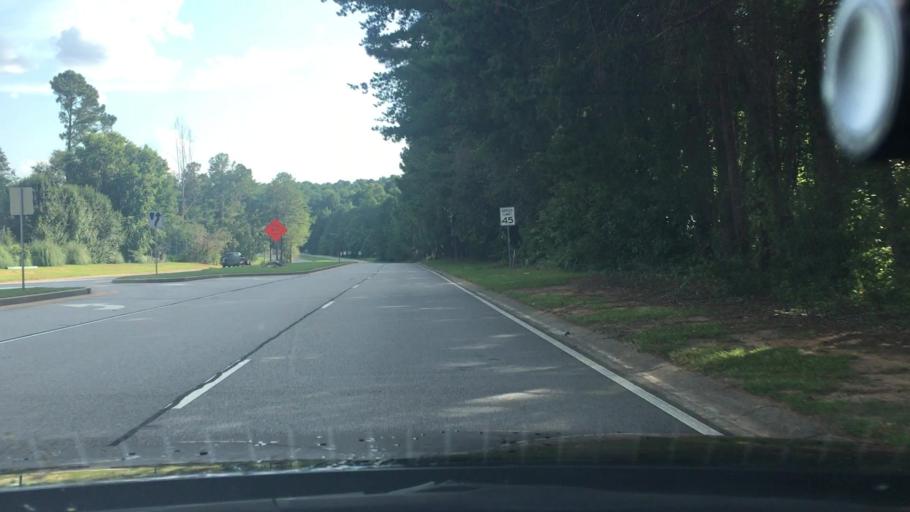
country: US
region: Georgia
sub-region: Coweta County
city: East Newnan
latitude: 33.3911
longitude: -84.7347
